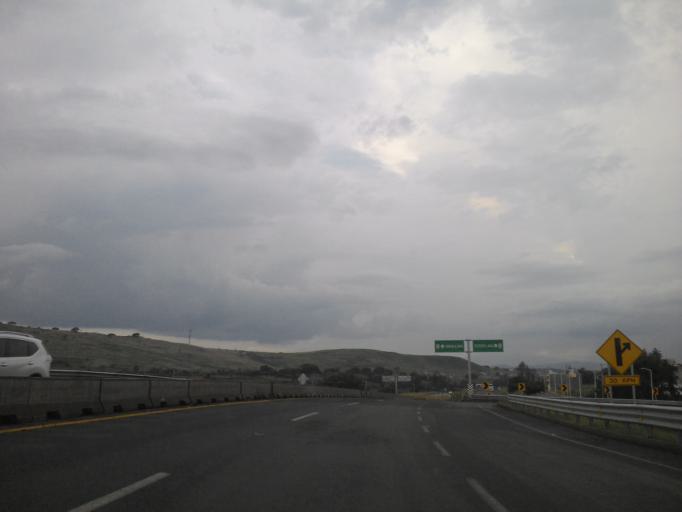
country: MX
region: Jalisco
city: Zapotlanejo
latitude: 20.6221
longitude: -103.0534
